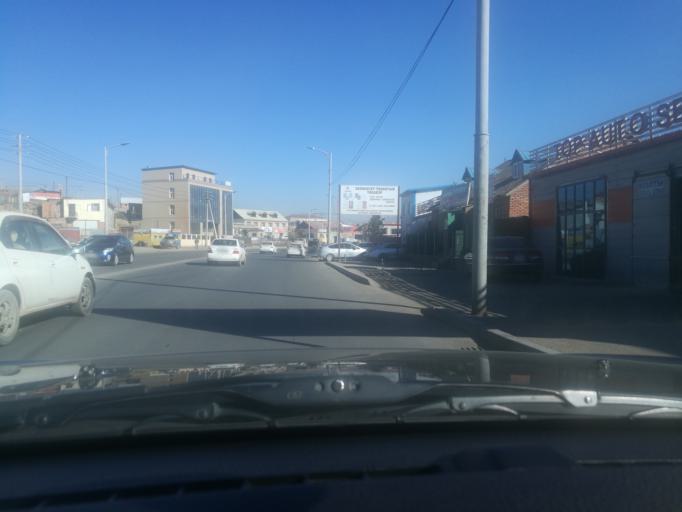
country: MN
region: Ulaanbaatar
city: Ulaanbaatar
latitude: 47.9379
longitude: 106.9096
